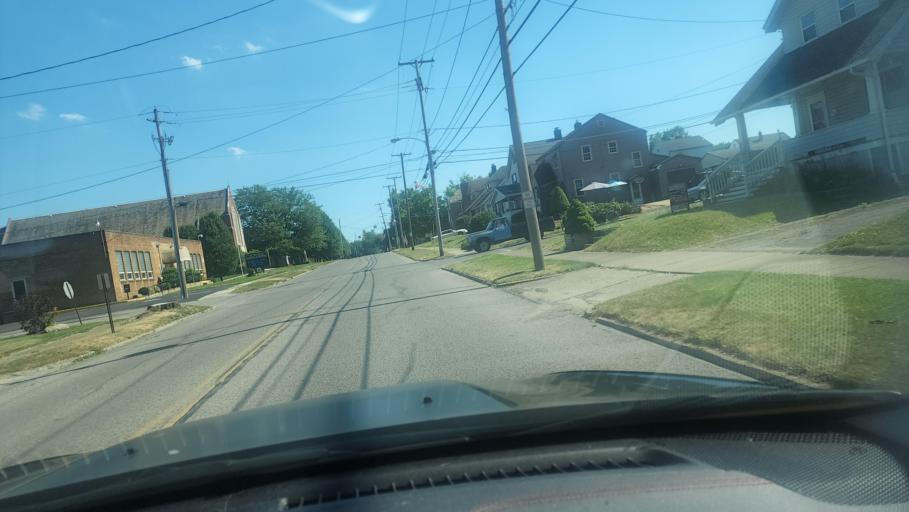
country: US
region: Ohio
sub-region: Mahoning County
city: Struthers
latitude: 41.0511
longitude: -80.6036
